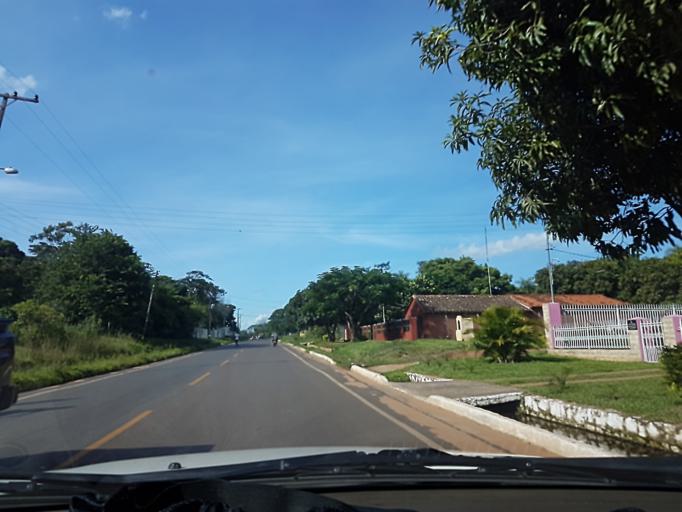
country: PY
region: Central
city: Limpio
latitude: -25.2230
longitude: -57.4485
